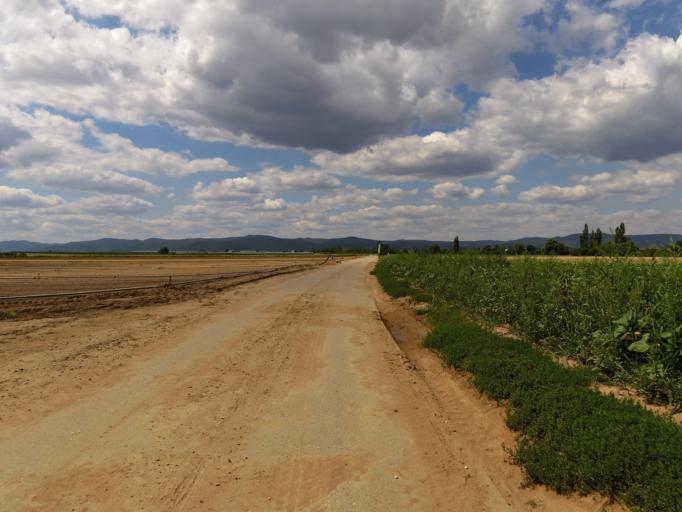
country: DE
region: Rheinland-Pfalz
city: Ellerstadt
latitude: 49.4505
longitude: 8.2681
